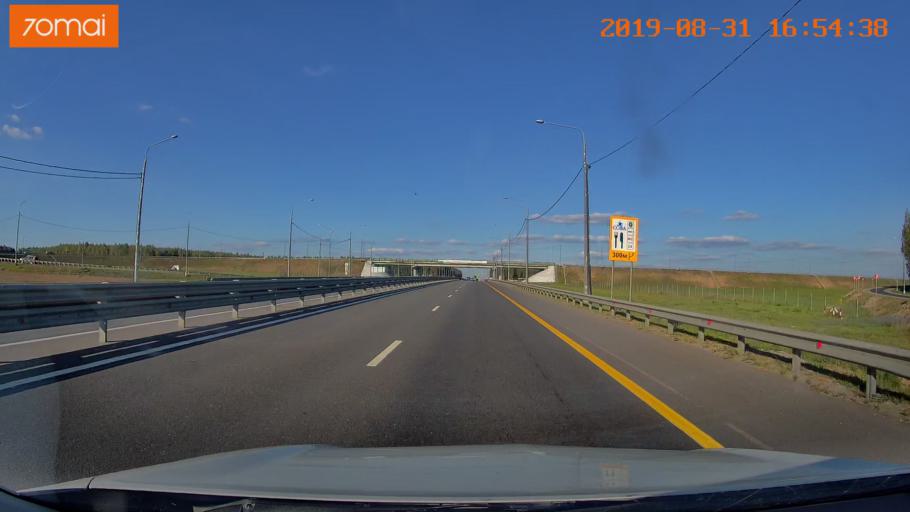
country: RU
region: Kaluga
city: Detchino
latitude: 54.7730
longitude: 36.2366
